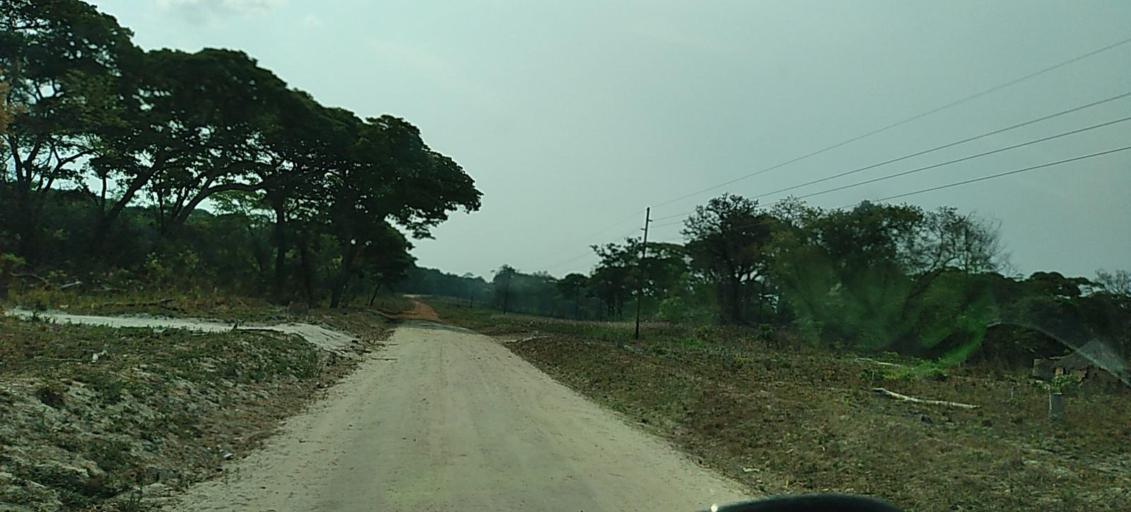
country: ZM
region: North-Western
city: Solwezi
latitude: -12.6959
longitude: 26.4070
